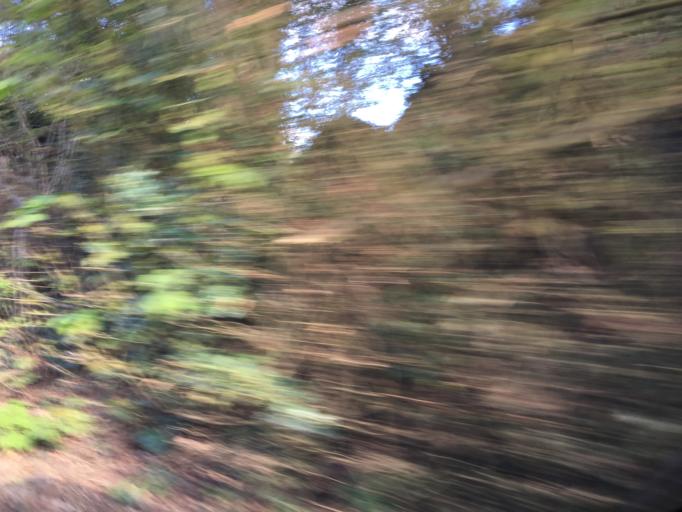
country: GB
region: Wales
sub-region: Torfaen County Borough
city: New Inn
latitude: 51.7103
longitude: -2.9668
